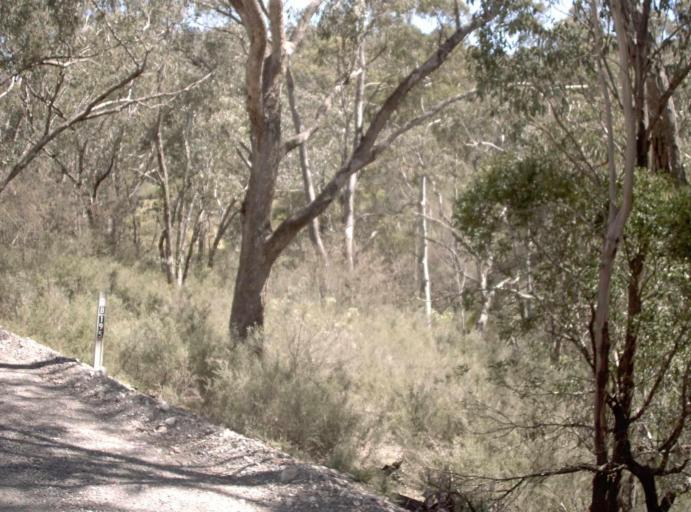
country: AU
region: New South Wales
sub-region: Bombala
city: Bombala
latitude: -37.1282
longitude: 148.6646
